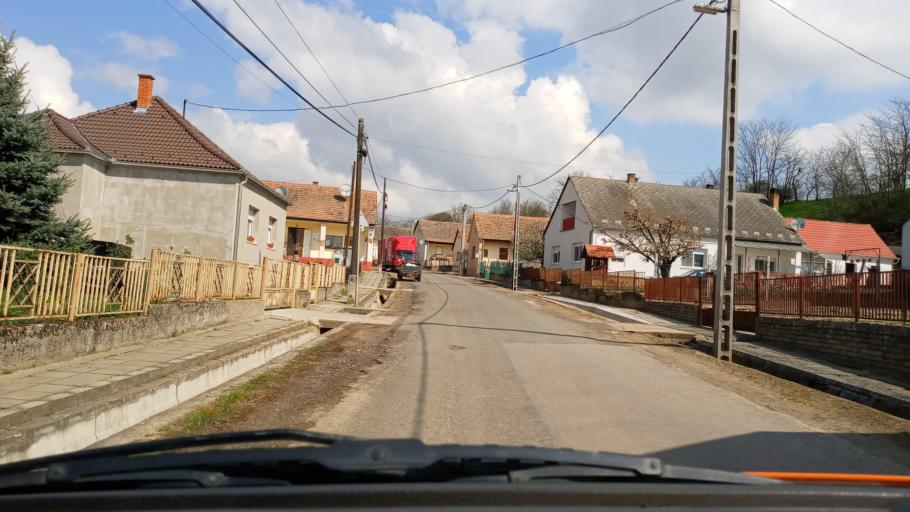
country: HU
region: Baranya
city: Boly
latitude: 46.0765
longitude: 18.5135
